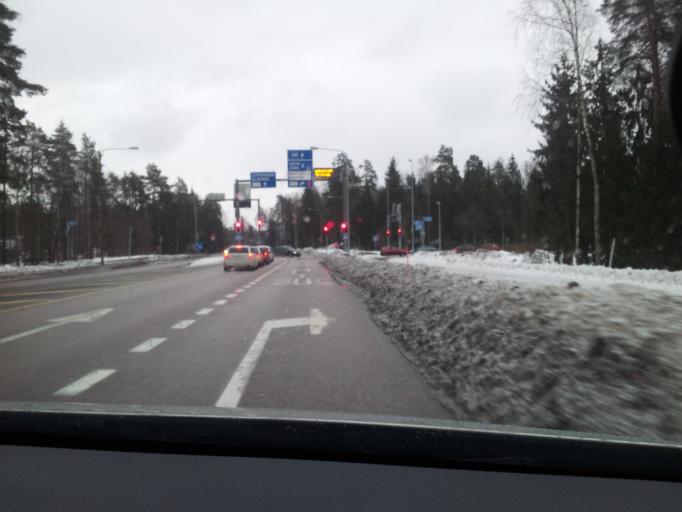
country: FI
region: Uusimaa
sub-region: Helsinki
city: Kauniainen
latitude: 60.2255
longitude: 24.7483
